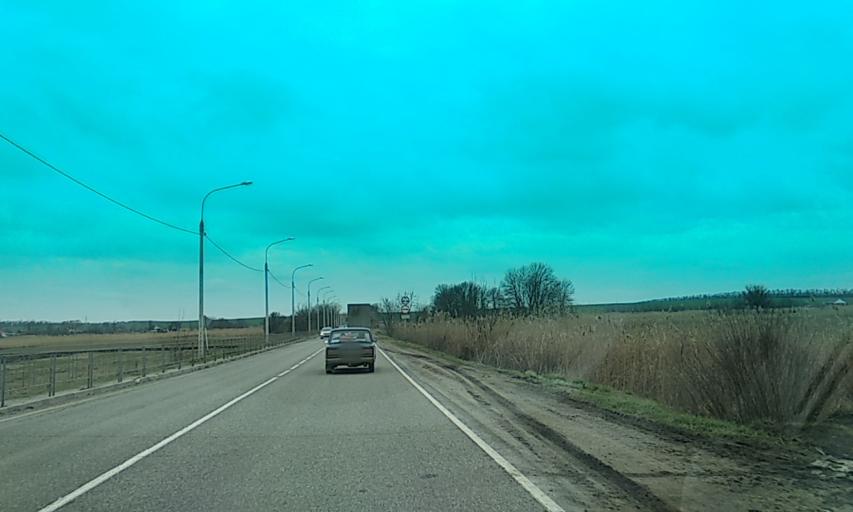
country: RU
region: Krasnodarskiy
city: Vyselki
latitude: 45.4832
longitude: 39.7080
